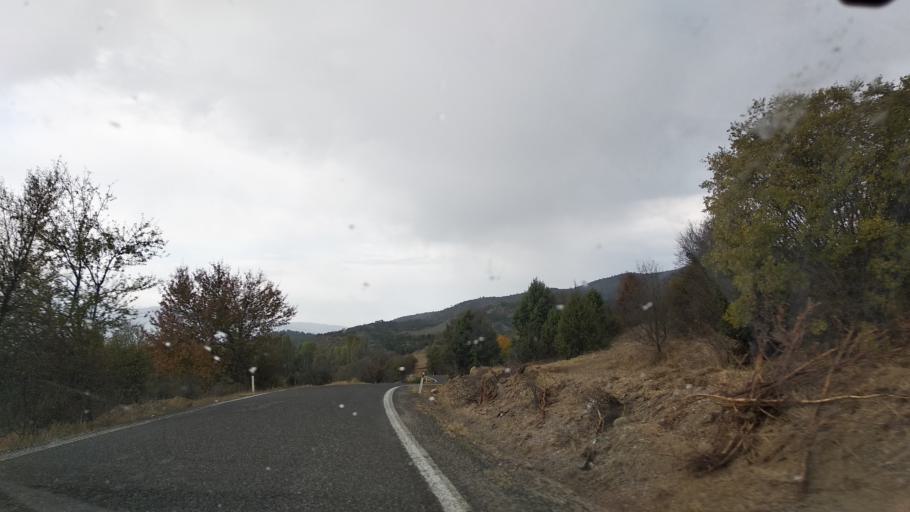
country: TR
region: Bolu
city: Seben
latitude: 40.3370
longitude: 31.4240
